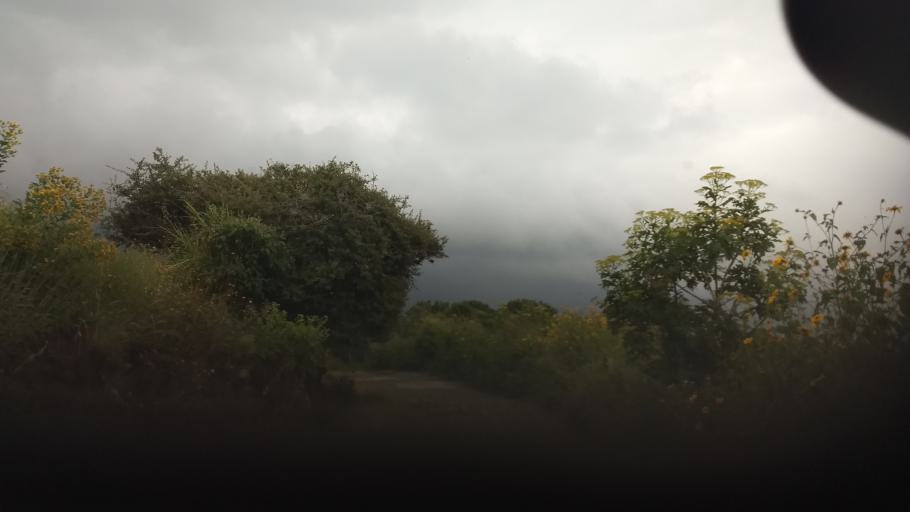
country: MX
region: Jalisco
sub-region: Tonila
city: San Marcos
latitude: 19.4660
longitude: -103.5339
